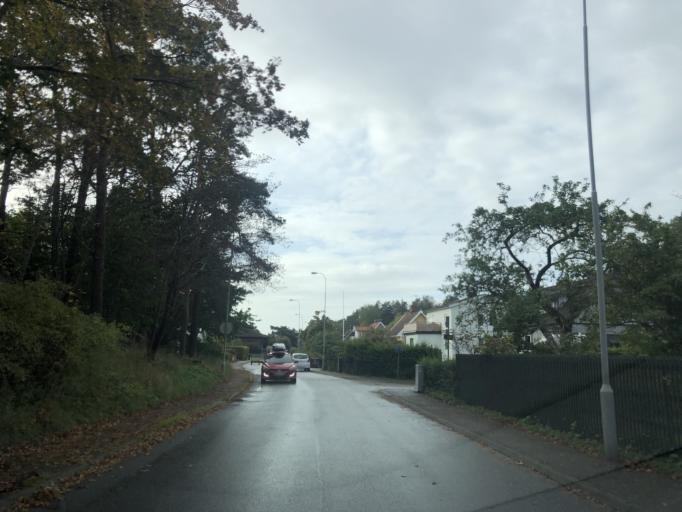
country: SE
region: Vaestra Goetaland
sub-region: Goteborg
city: Majorna
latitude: 57.6691
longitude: 11.8955
